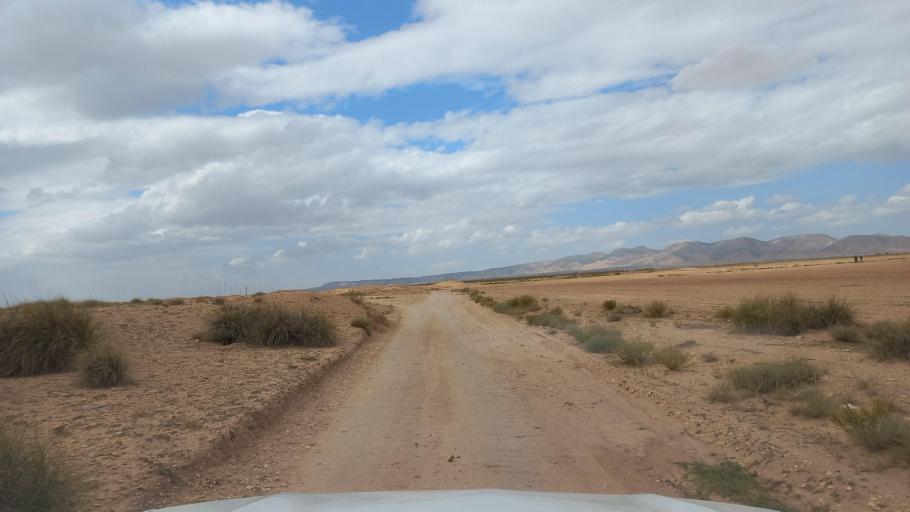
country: TN
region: Al Qasrayn
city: Sbiba
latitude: 35.3791
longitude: 9.1041
